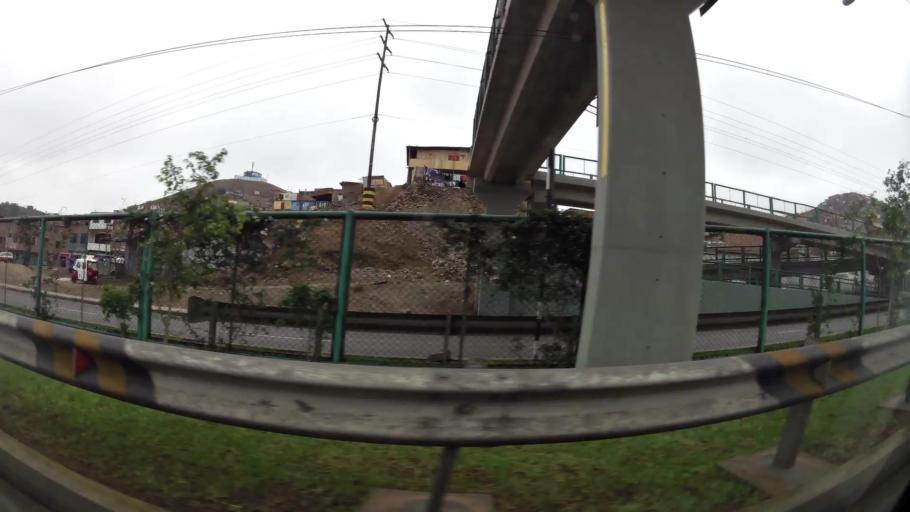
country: PE
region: Lima
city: Ventanilla
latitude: -11.8668
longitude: -77.1283
